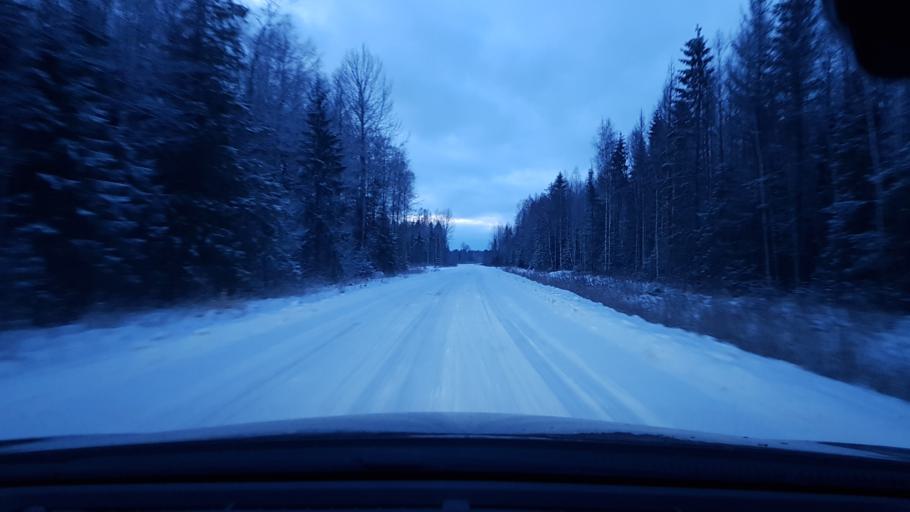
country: EE
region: Harju
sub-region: Nissi vald
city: Turba
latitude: 59.1236
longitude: 24.0933
